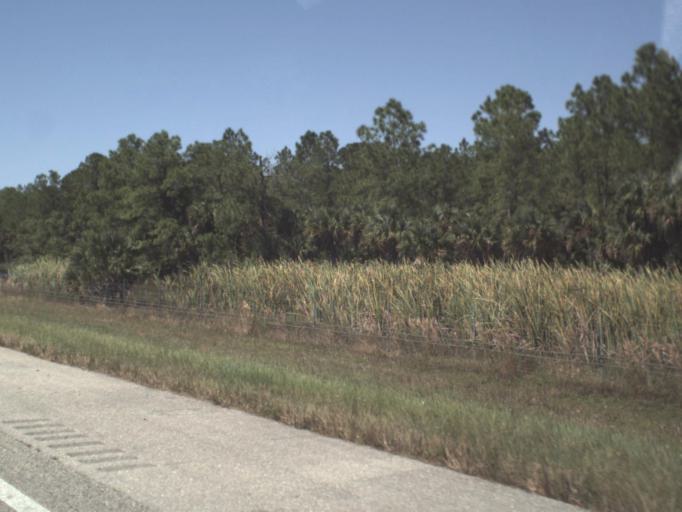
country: US
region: Florida
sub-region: Collier County
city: Golden Gate
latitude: 26.1534
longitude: -81.5775
